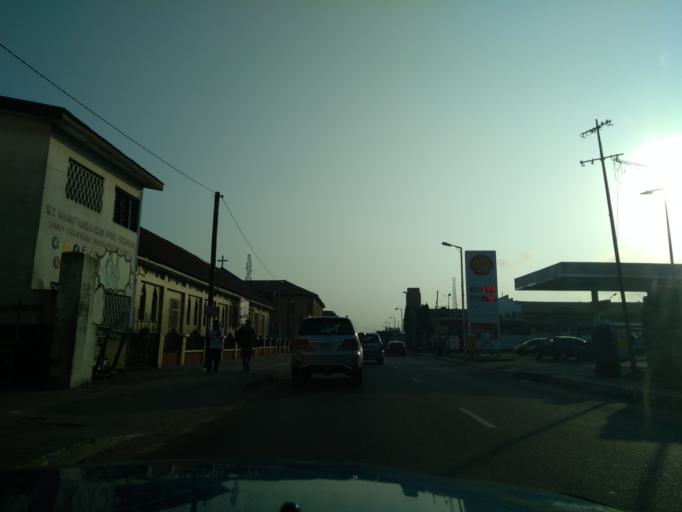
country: GH
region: Greater Accra
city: Accra
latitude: 5.5412
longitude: -0.2130
